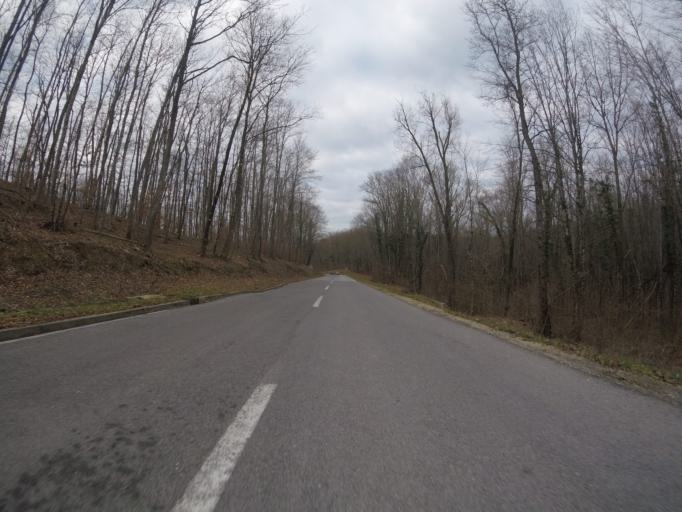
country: HR
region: Sisacko-Moslavacka
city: Glina
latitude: 45.4868
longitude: 16.0397
